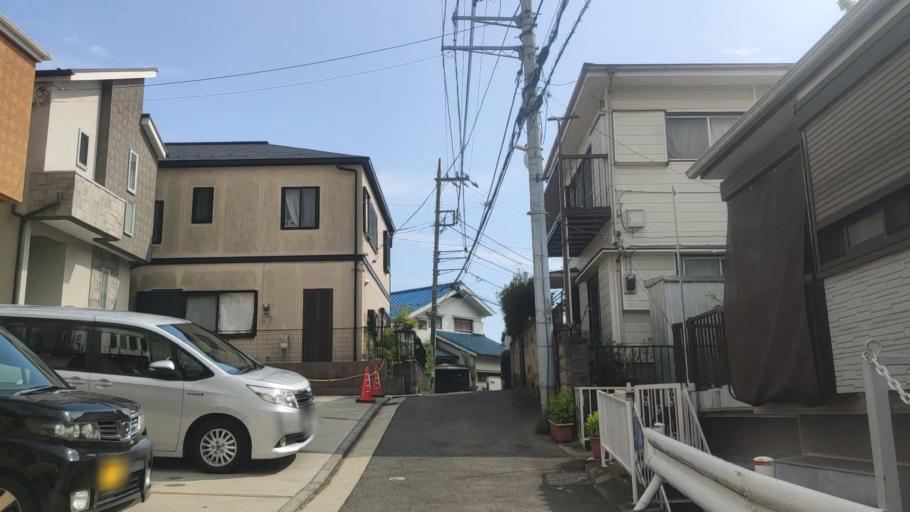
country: JP
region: Kanagawa
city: Yokohama
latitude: 35.4238
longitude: 139.6155
